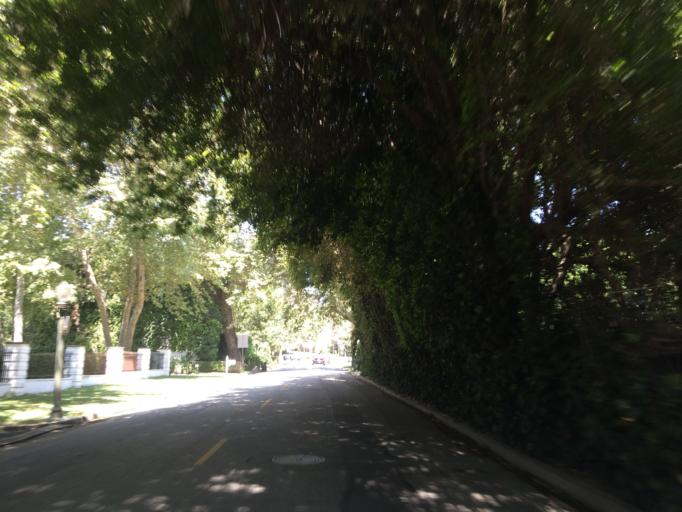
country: US
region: California
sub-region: Los Angeles County
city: Westwood, Los Angeles
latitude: 34.0843
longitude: -118.4445
